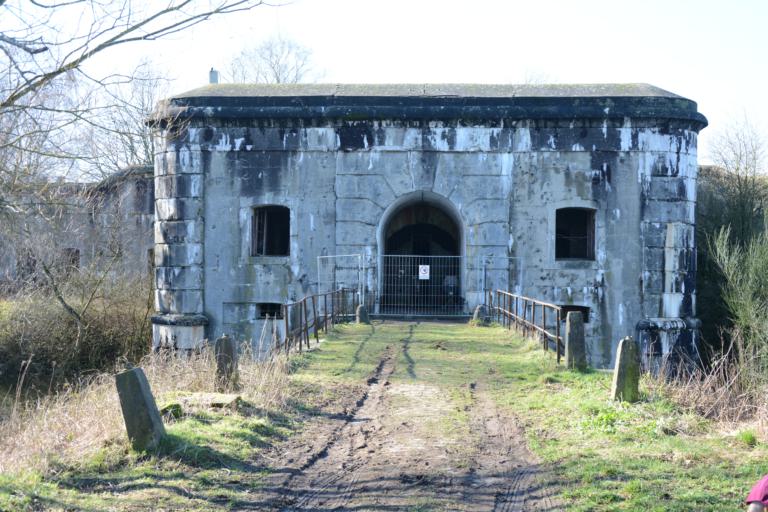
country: BE
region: Flanders
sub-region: Provincie Oost-Vlaanderen
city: Beveren
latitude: 51.1730
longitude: 4.2306
